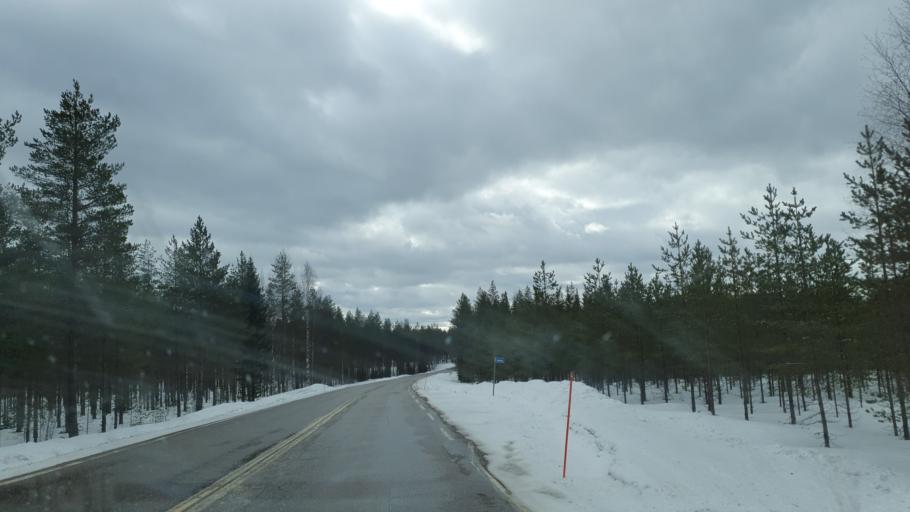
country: FI
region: Kainuu
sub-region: Kehys-Kainuu
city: Puolanka
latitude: 65.0528
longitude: 27.7166
